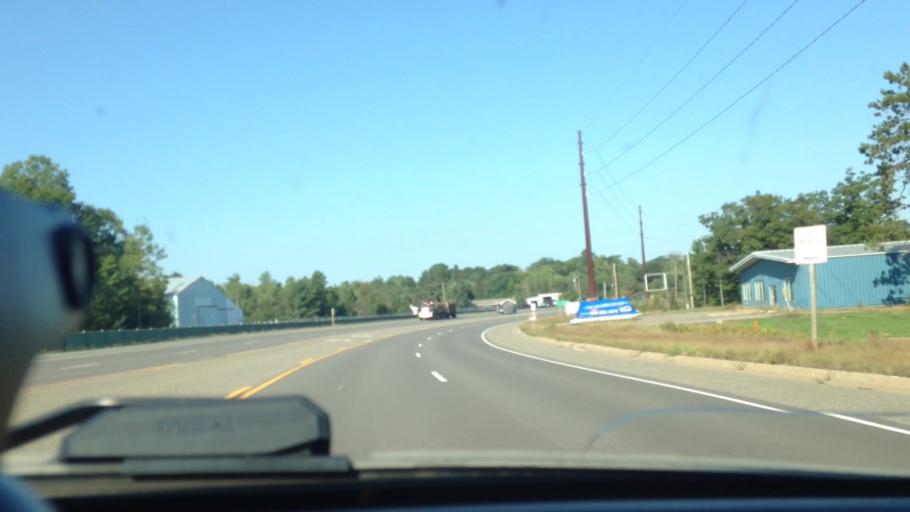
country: US
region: Michigan
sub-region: Dickinson County
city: Iron Mountain
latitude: 45.8820
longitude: -88.1385
